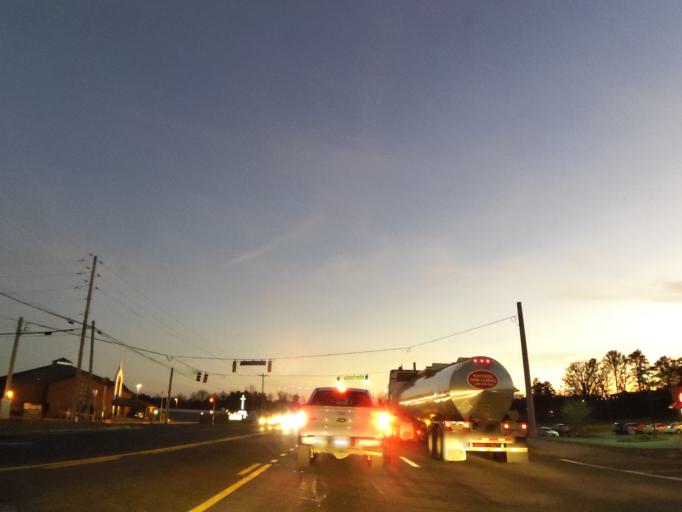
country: US
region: Georgia
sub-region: Whitfield County
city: Dalton
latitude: 34.8334
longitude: -84.9434
